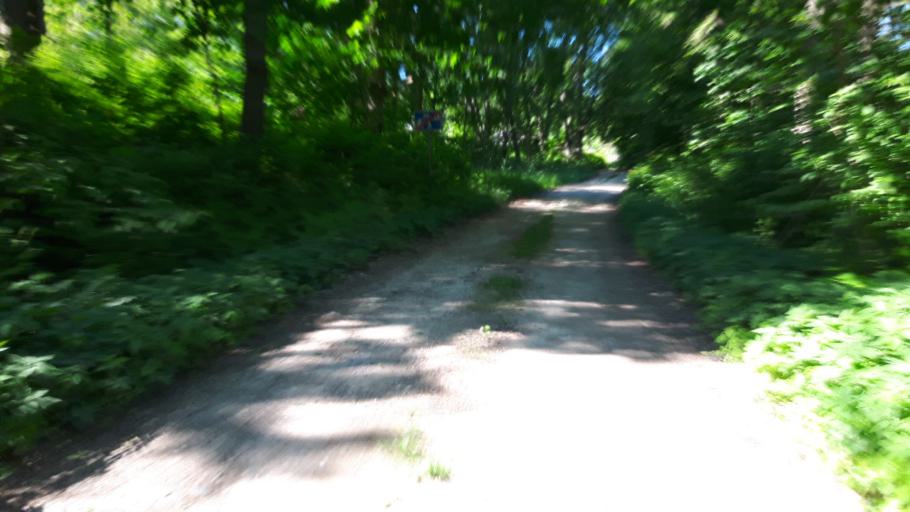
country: EE
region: Harju
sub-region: Loksa linn
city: Loksa
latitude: 59.5672
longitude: 25.8460
